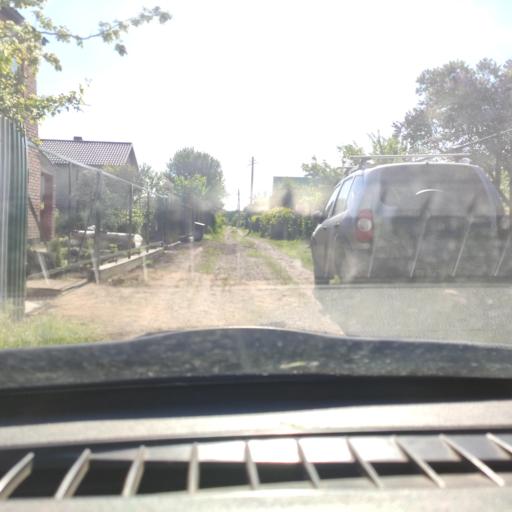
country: RU
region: Samara
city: Tol'yatti
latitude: 53.6273
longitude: 49.4044
